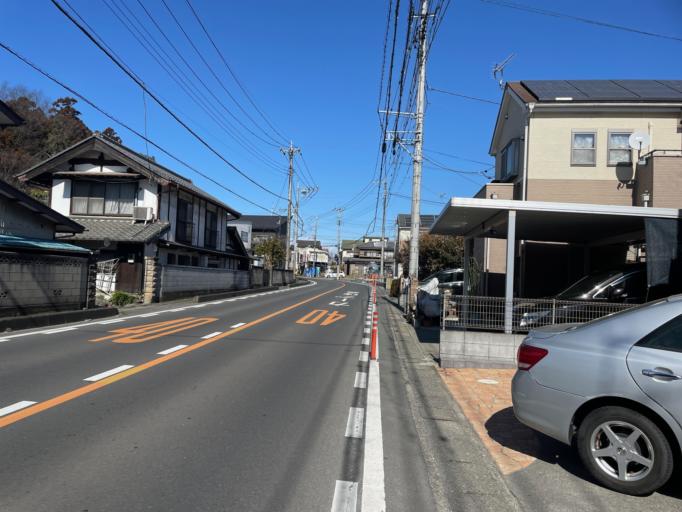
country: JP
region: Saitama
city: Sakado
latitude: 35.9534
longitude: 139.4345
